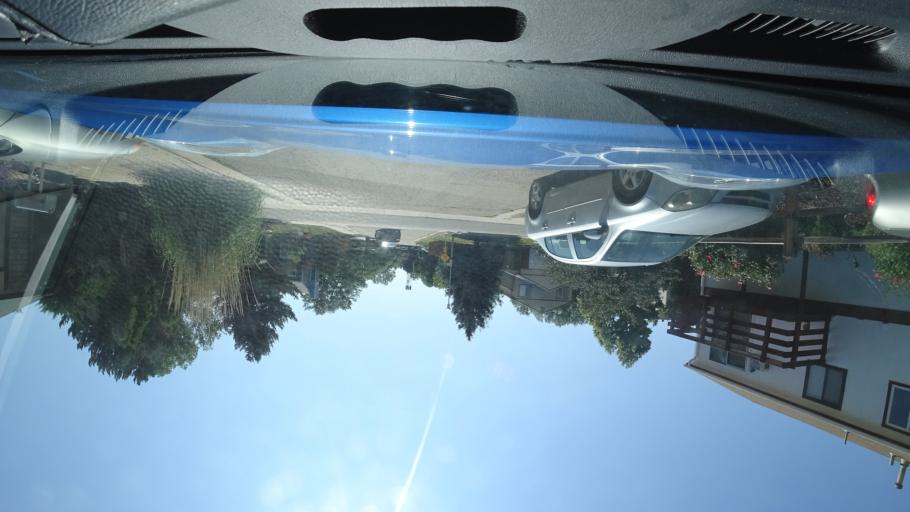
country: US
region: Colorado
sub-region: Adams County
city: Aurora
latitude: 39.6877
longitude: -104.8225
